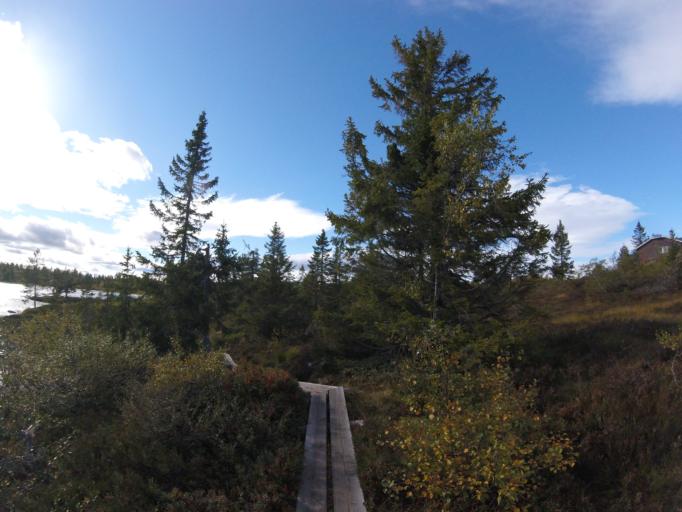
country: NO
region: Buskerud
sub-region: Flesberg
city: Lampeland
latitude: 59.7675
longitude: 9.4113
